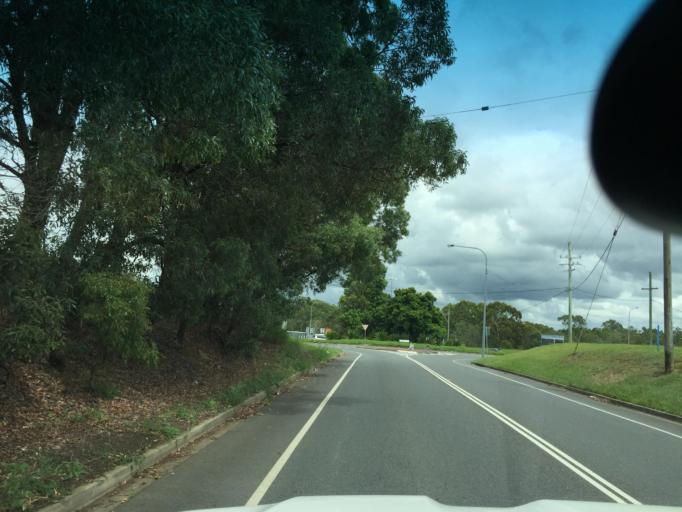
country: AU
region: Queensland
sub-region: Moreton Bay
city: Morayfield
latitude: -27.1087
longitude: 152.9700
